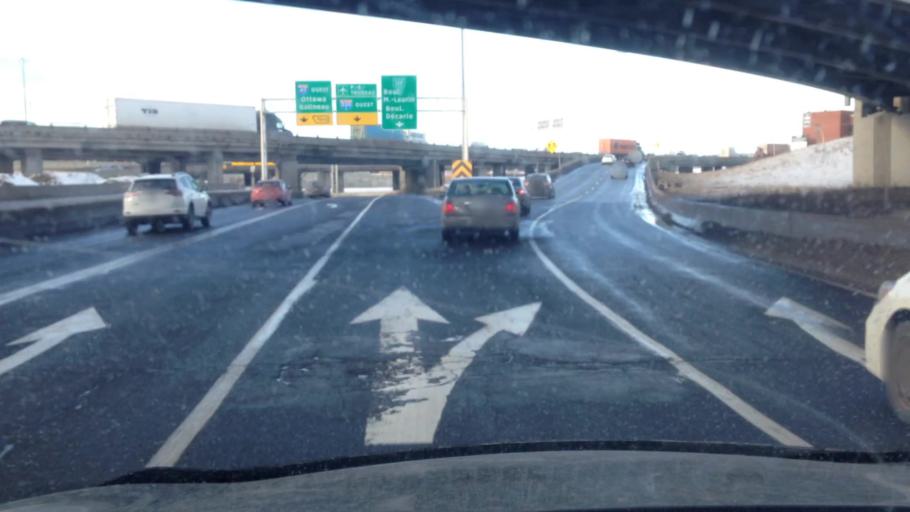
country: CA
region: Quebec
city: Saint-Laurent
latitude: 45.5023
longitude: -73.6636
